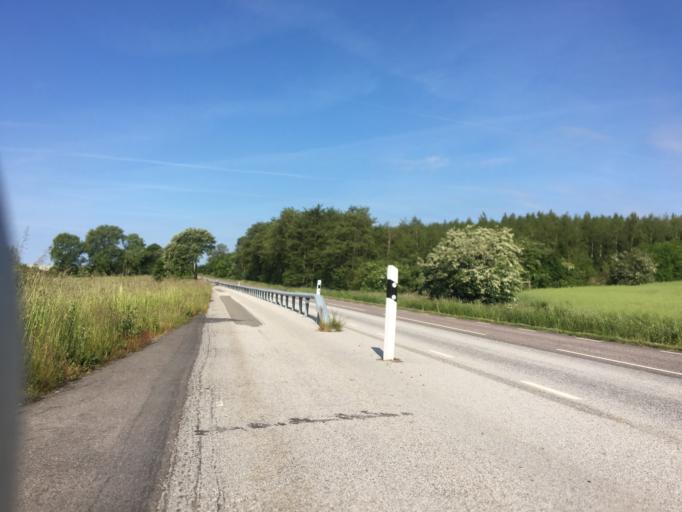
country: SE
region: Skane
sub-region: Skurups Kommun
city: Rydsgard
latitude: 55.4185
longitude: 13.6815
